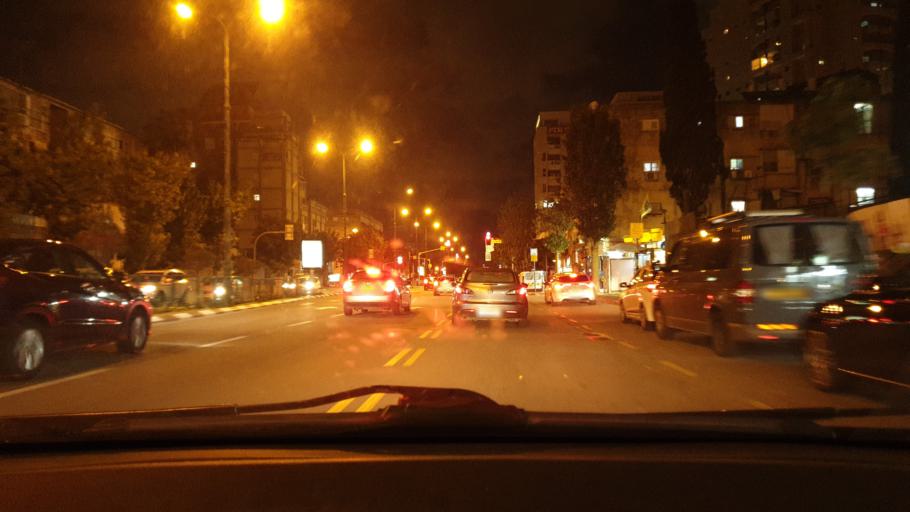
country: IL
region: Central District
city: Rishon LeZiyyon
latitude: 31.9596
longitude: 34.8025
